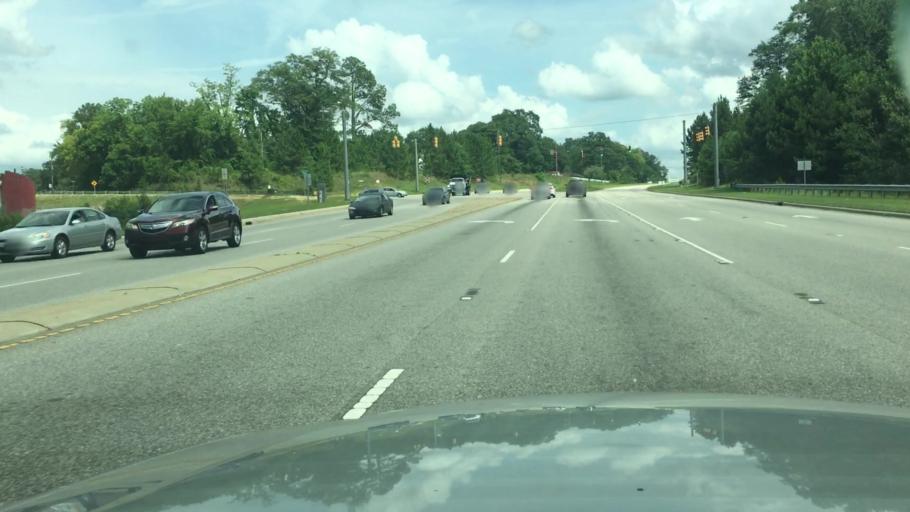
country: US
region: North Carolina
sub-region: Cumberland County
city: Hope Mills
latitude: 35.0020
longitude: -78.9772
